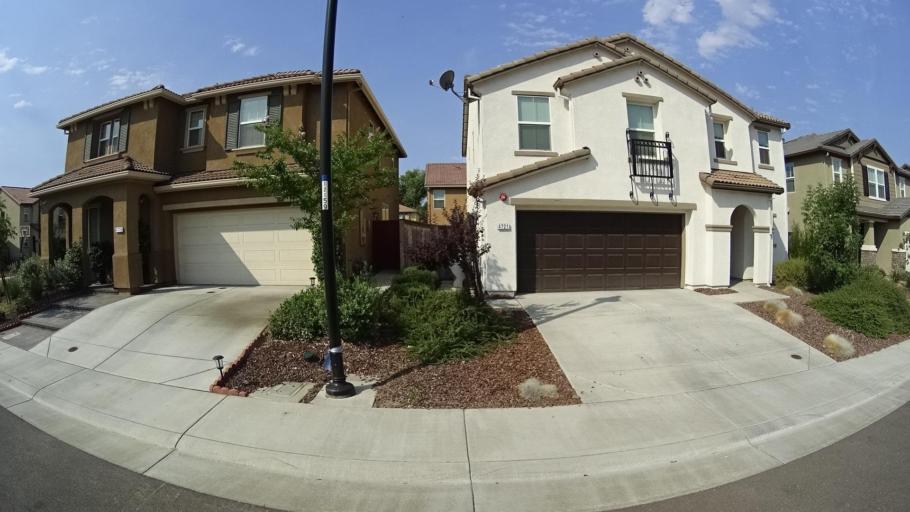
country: US
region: California
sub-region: Placer County
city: Rocklin
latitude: 38.8014
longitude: -121.2129
